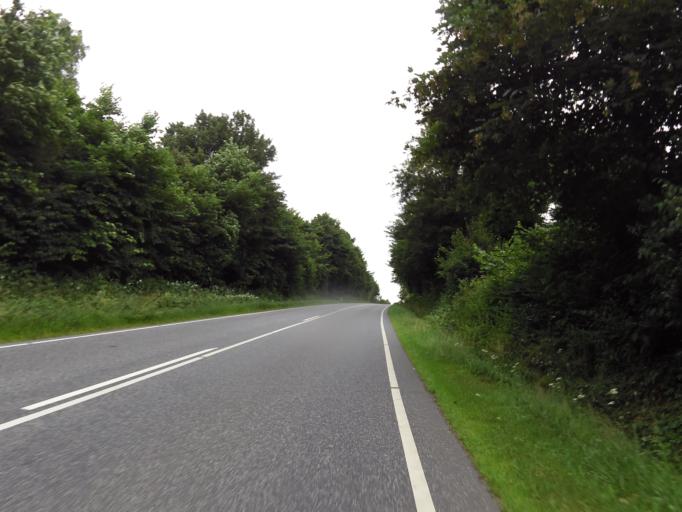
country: DK
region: South Denmark
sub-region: Tonder Kommune
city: Logumkloster
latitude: 55.1594
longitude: 8.9616
